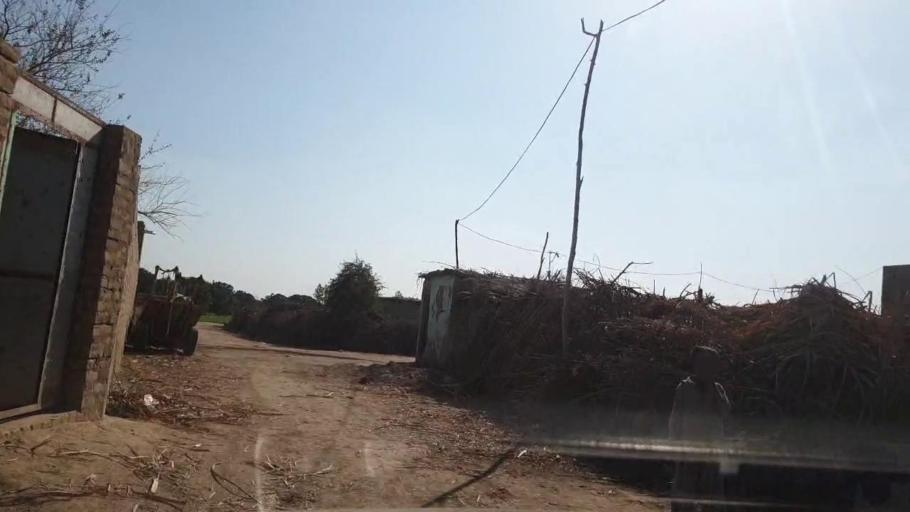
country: PK
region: Sindh
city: Tando Allahyar
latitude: 25.4811
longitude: 68.6769
